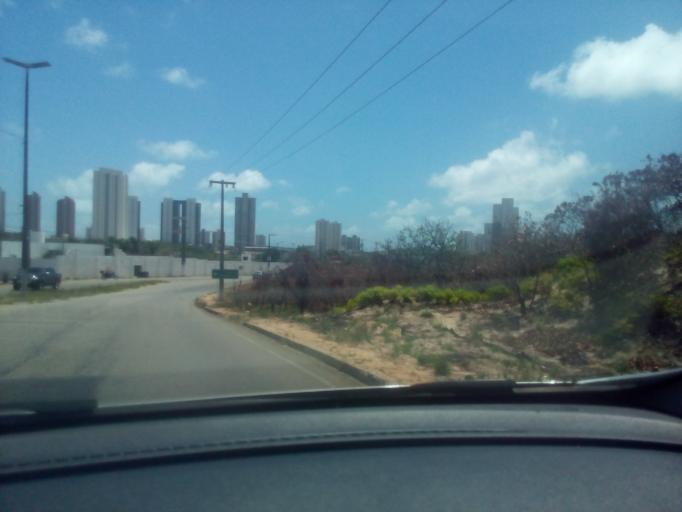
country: BR
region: Rio Grande do Norte
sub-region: Parnamirim
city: Parnamirim
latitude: -5.8871
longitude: -35.1890
